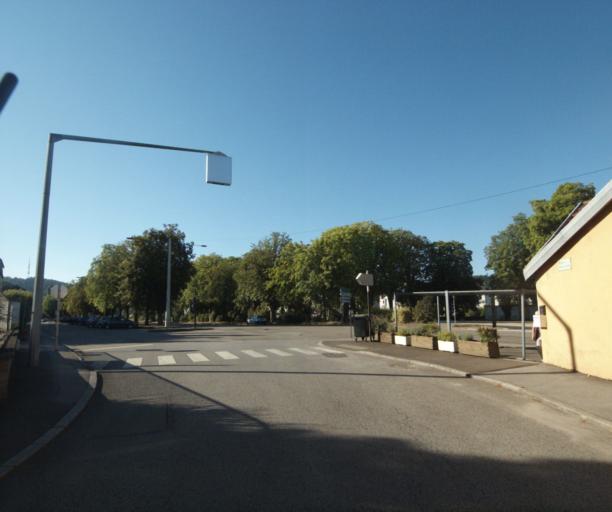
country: FR
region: Lorraine
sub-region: Departement des Vosges
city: Chantraine
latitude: 48.1680
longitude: 6.4502
